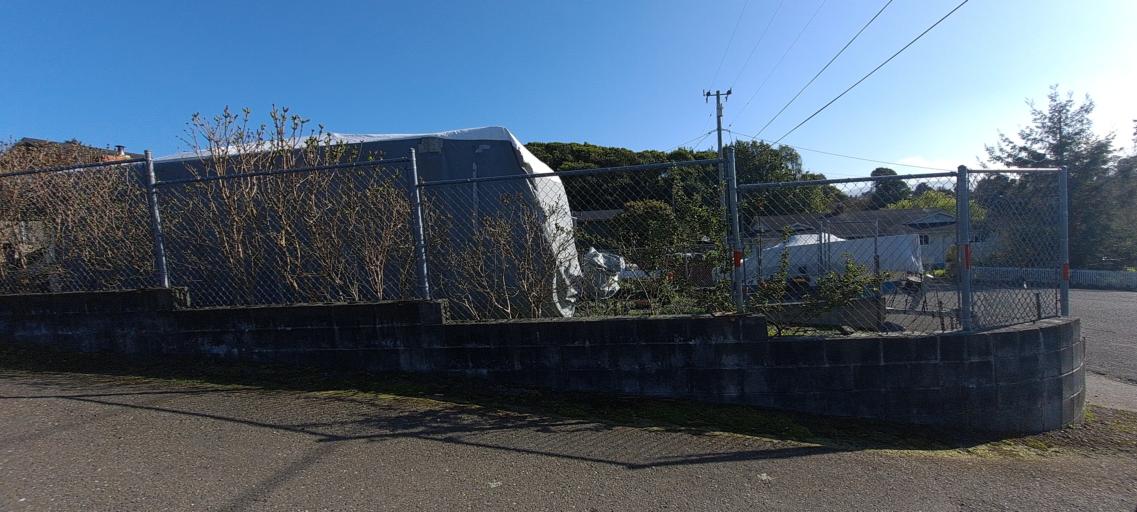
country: US
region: California
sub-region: Humboldt County
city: Fortuna
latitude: 40.5762
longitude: -124.1402
